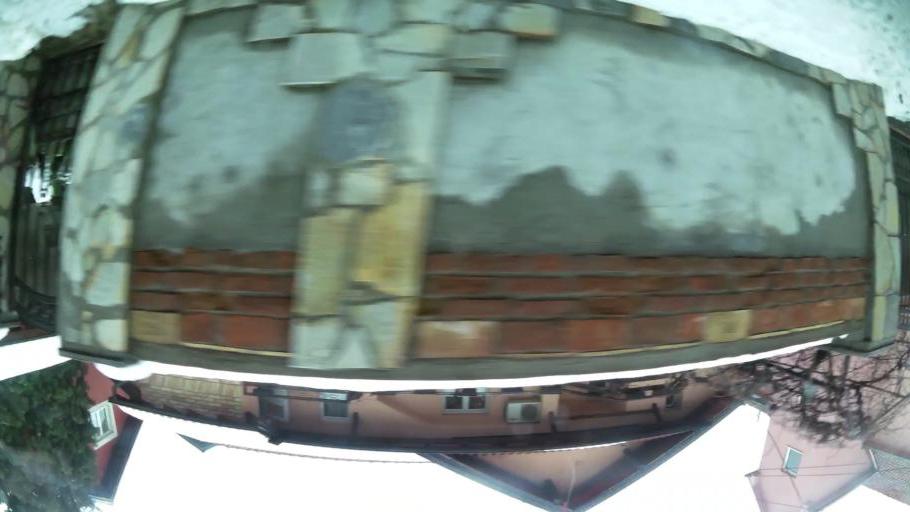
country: RS
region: Central Serbia
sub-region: Belgrade
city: Zemun
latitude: 44.8433
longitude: 20.3616
